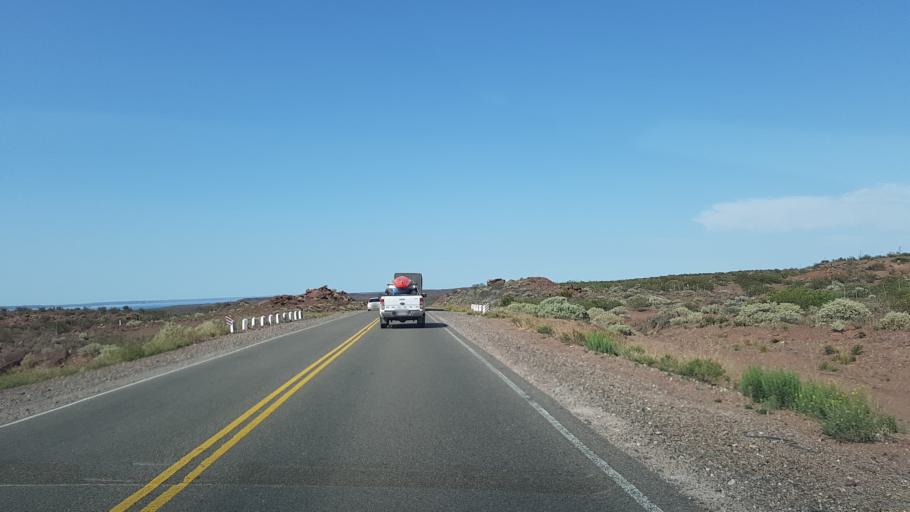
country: AR
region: Neuquen
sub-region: Departamento de Picun Leufu
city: Picun Leufu
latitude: -39.2761
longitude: -68.8561
